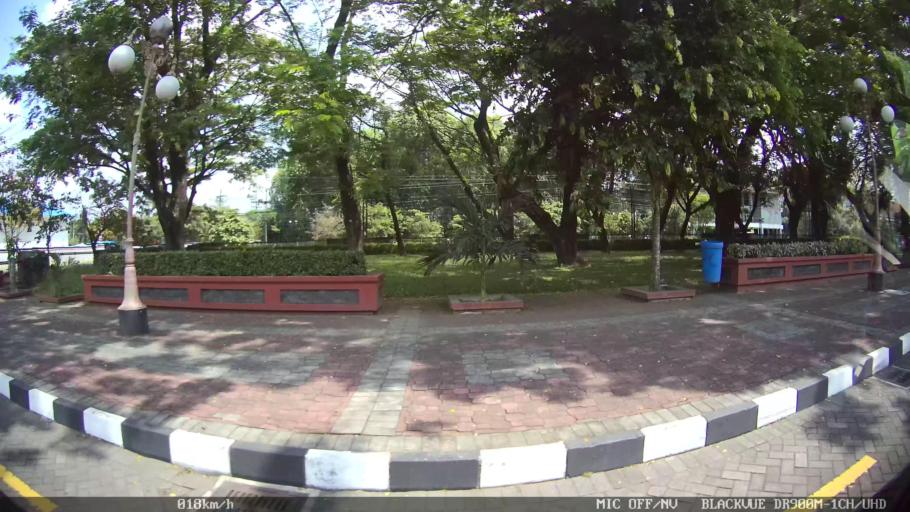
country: ID
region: Daerah Istimewa Yogyakarta
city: Yogyakarta
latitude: -7.7726
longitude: 110.3780
